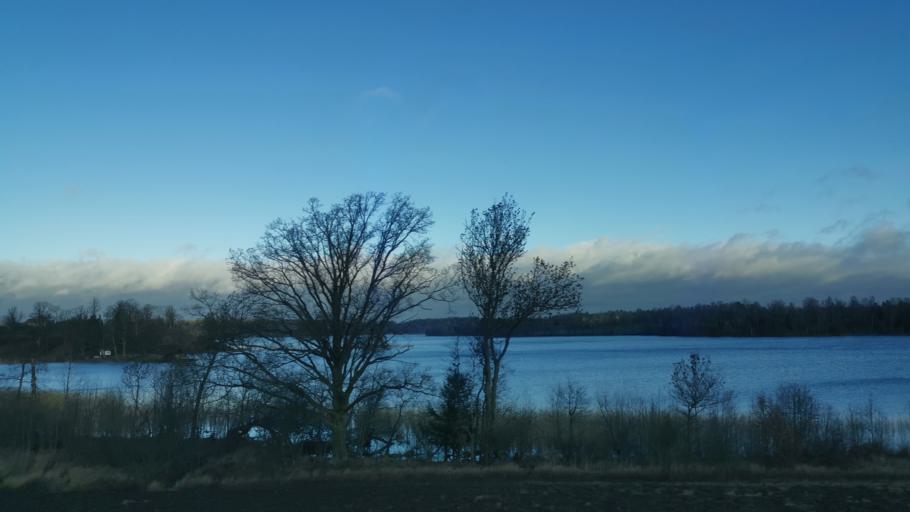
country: SE
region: Soedermanland
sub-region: Strangnas Kommun
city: Akers Styckebruk
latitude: 59.0871
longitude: 16.9860
